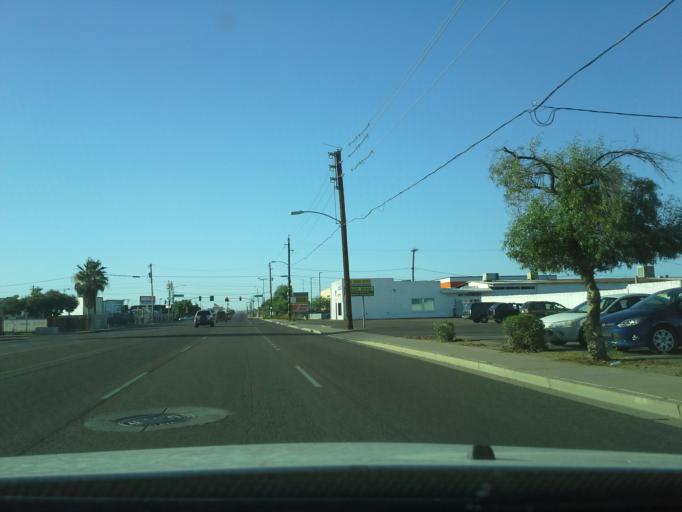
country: US
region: Arizona
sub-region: Maricopa County
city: Phoenix
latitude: 33.4350
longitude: -112.1000
